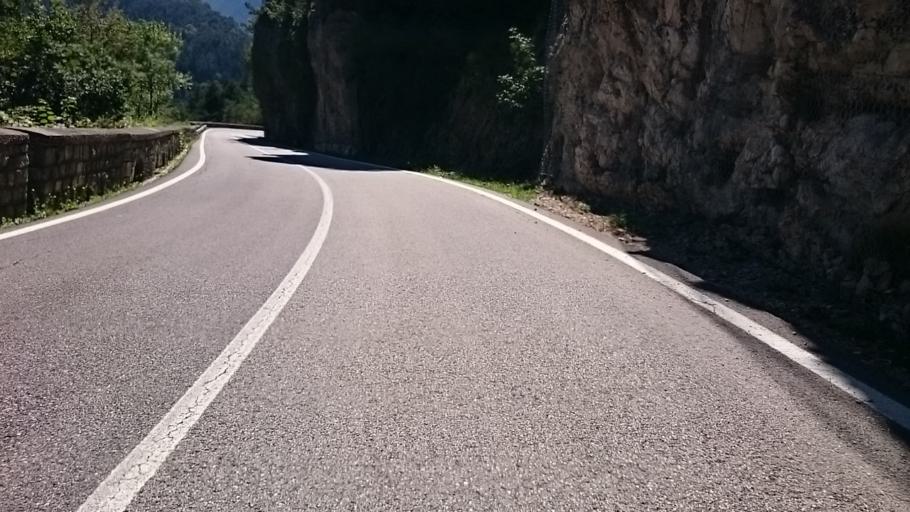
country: IT
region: Veneto
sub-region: Provincia di Belluno
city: Perarolo di Cadore
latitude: 46.4035
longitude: 12.3684
